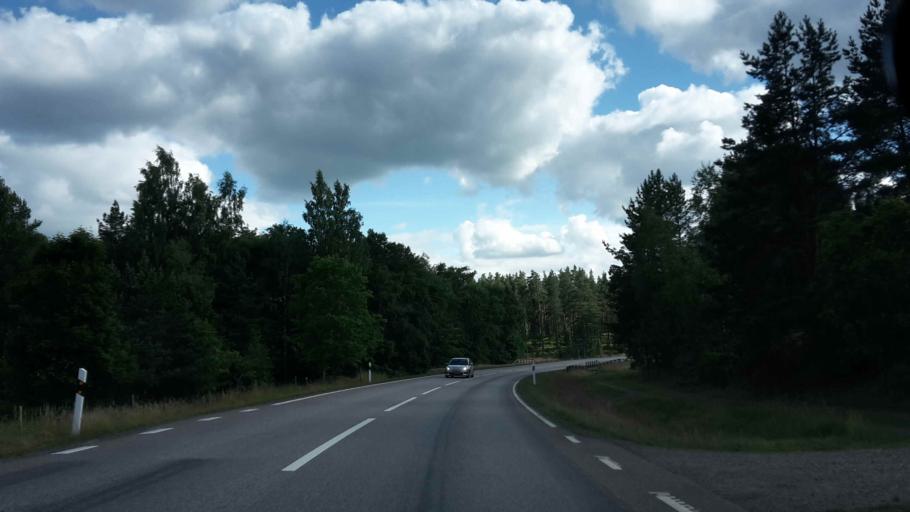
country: SE
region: OErebro
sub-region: Hallsbergs Kommun
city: Palsboda
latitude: 58.8641
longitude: 15.4128
